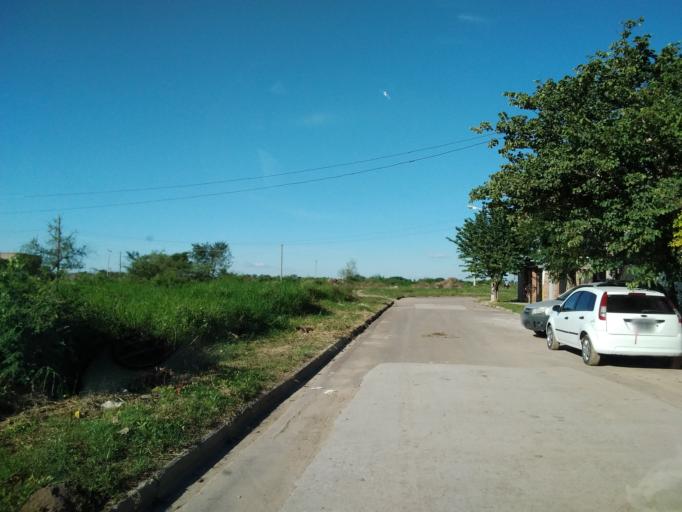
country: AR
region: Corrientes
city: Corrientes
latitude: -27.4563
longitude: -58.7683
